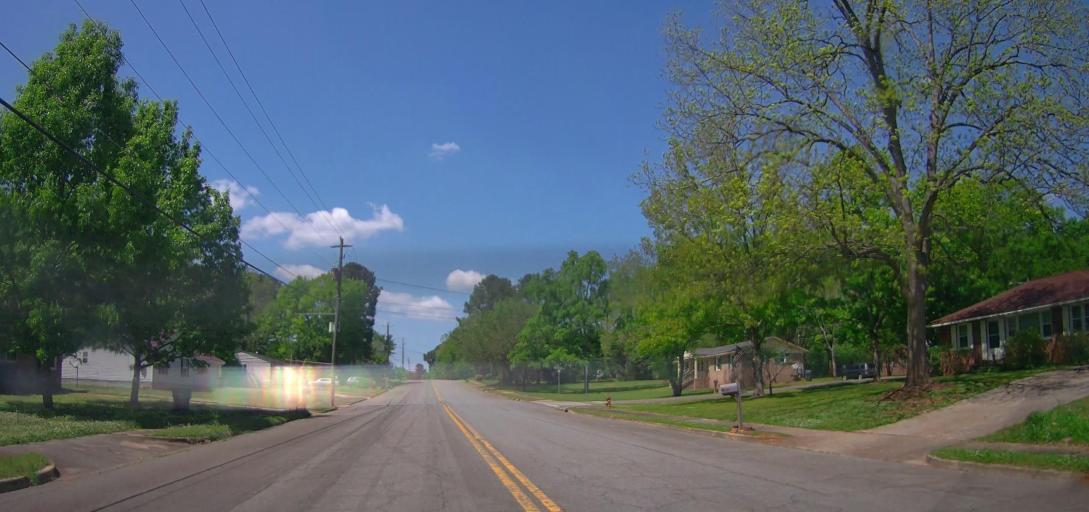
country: US
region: Georgia
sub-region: Putnam County
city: Eatonton
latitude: 33.3244
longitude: -83.4006
